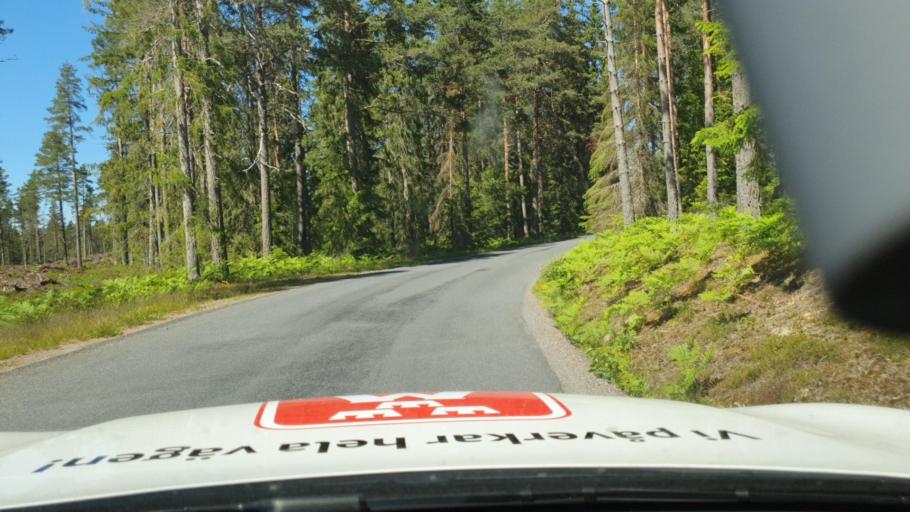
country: SE
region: Joenkoeping
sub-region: Habo Kommun
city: Habo
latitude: 57.9713
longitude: 14.0343
